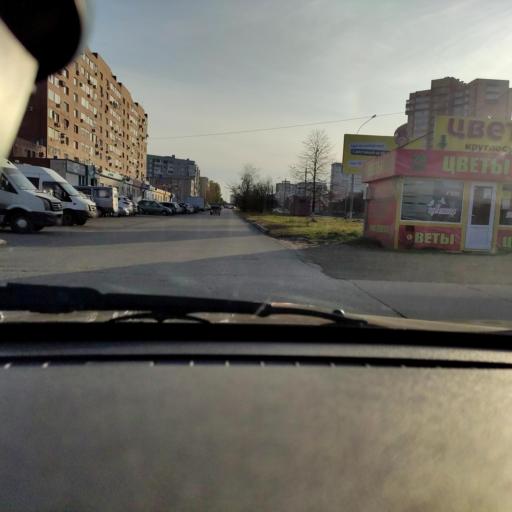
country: RU
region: Samara
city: Tol'yatti
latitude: 53.5419
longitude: 49.3385
